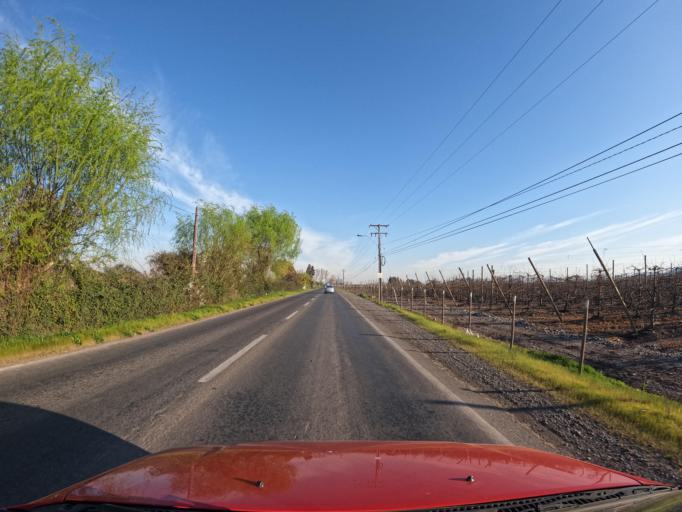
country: CL
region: Maule
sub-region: Provincia de Curico
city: Rauco
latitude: -34.8945
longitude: -71.2739
